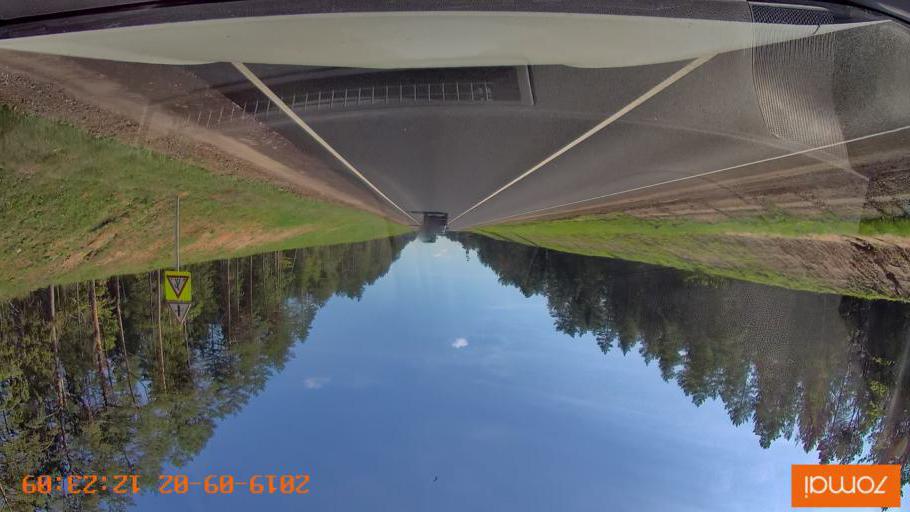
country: RU
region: Smolensk
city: Shumyachi
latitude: 53.8762
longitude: 32.6235
